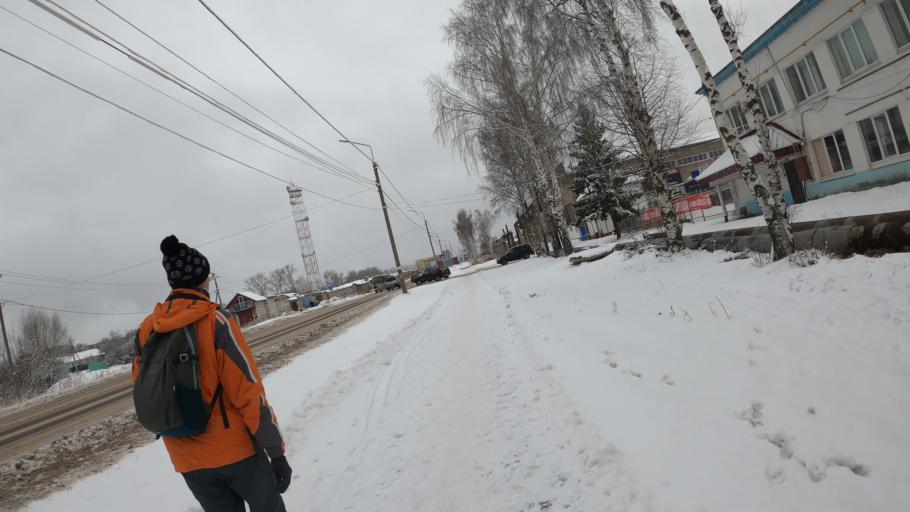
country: RU
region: Jaroslavl
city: Pereslavl'-Zalesskiy
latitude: 56.7430
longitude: 38.8914
